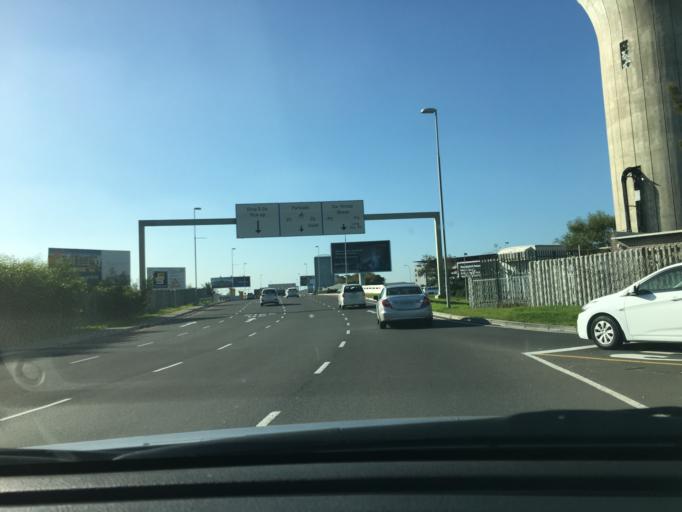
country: ZA
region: Western Cape
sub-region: City of Cape Town
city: Lansdowne
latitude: -33.9681
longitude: 18.5917
